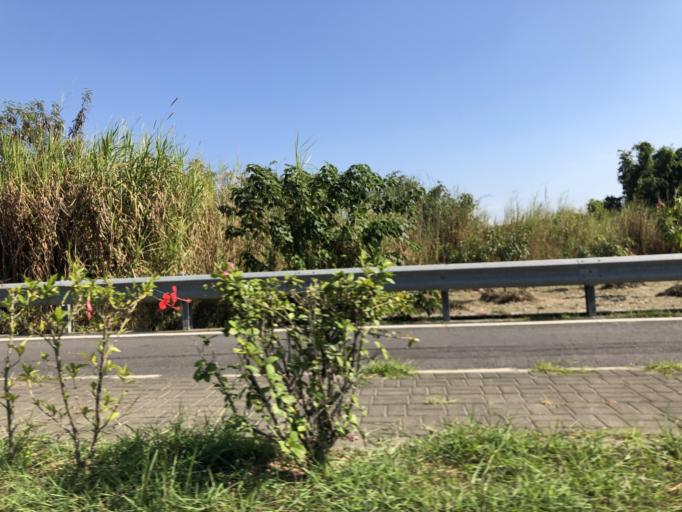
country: TW
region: Taiwan
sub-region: Tainan
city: Tainan
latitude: 23.0319
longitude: 120.3225
